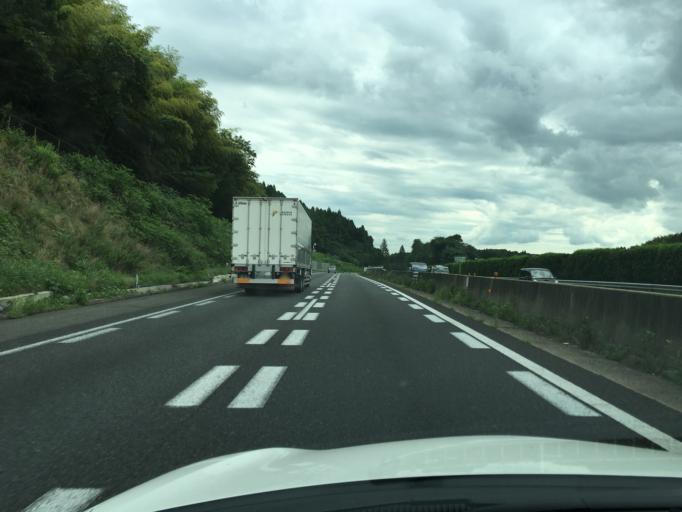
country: JP
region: Fukushima
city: Nihommatsu
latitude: 37.6048
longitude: 140.4217
